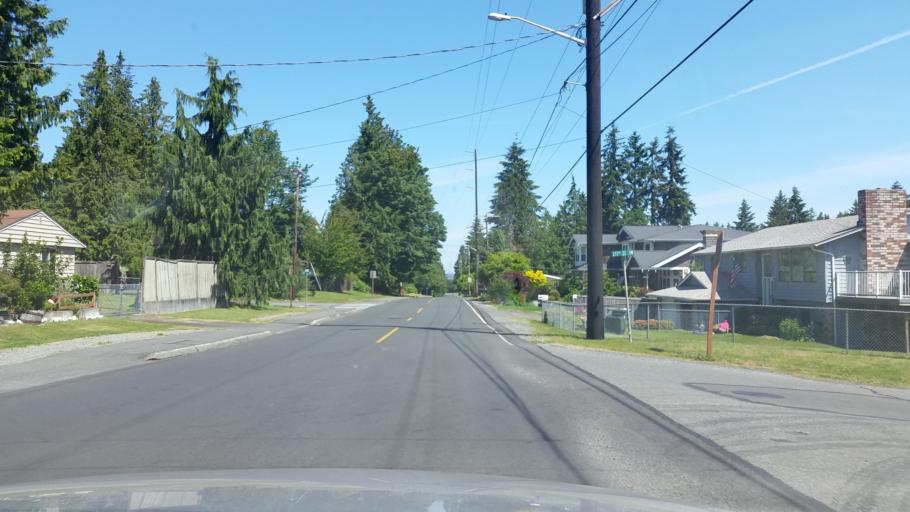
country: US
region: Washington
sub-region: Snohomish County
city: Esperance
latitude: 47.8023
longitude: -122.3615
